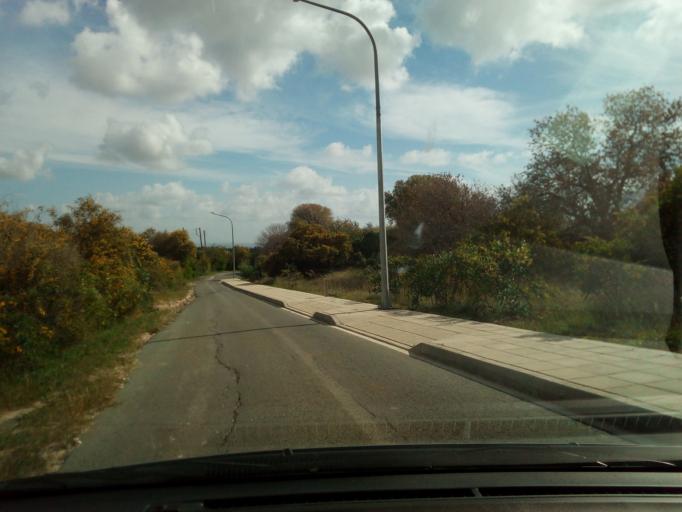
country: CY
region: Pafos
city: Paphos
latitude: 34.7669
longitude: 32.4655
